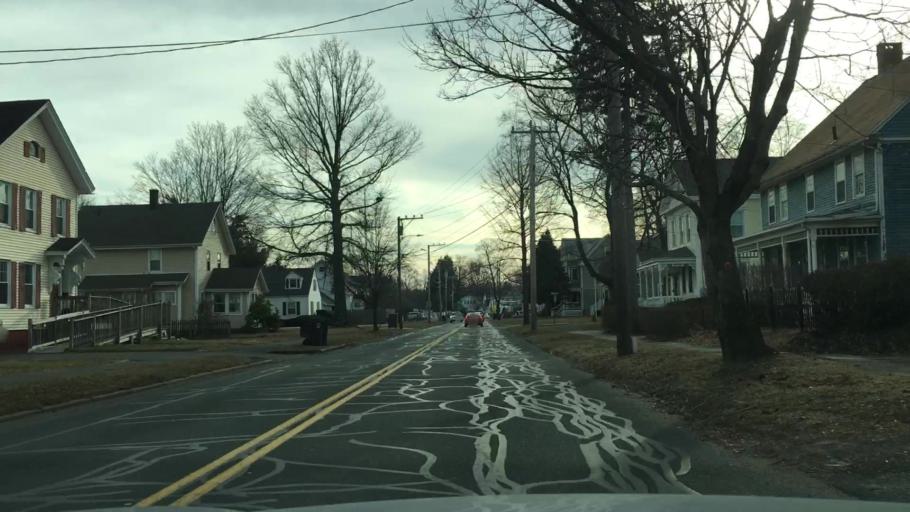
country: US
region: Massachusetts
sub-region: Hampden County
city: Westfield
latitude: 42.1168
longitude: -72.7522
